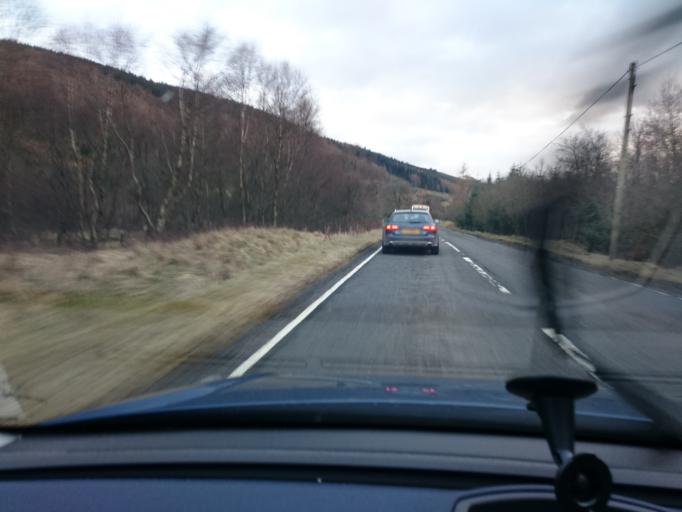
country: GB
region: Scotland
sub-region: Stirling
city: Callander
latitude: 56.3669
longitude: -4.2994
